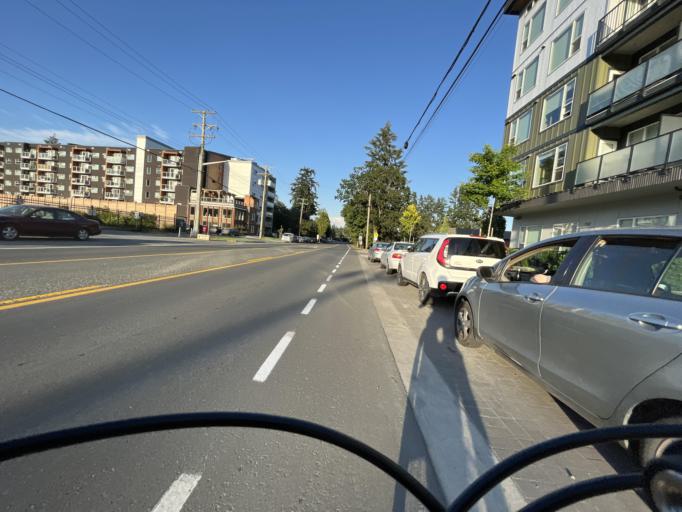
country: CA
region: British Columbia
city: Langford
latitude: 48.4496
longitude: -123.5169
